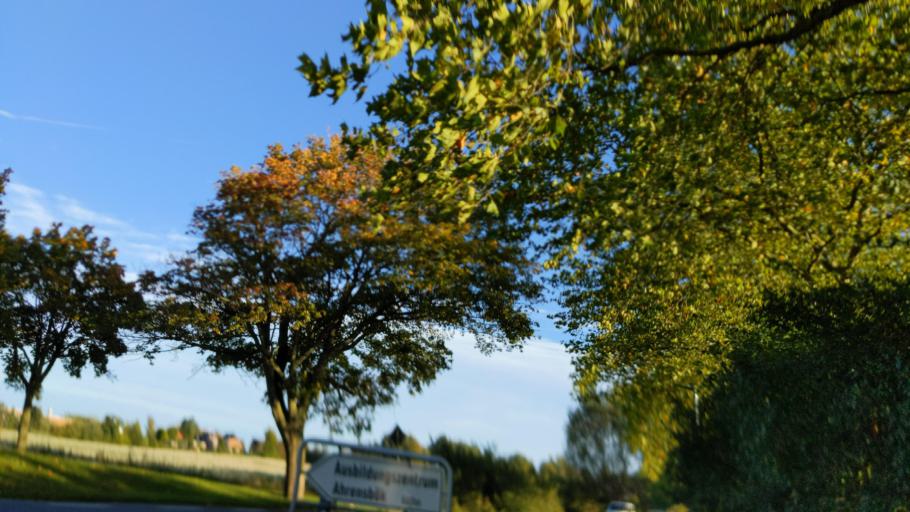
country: DE
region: Schleswig-Holstein
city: Ahrensbok
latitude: 54.0220
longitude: 10.5672
